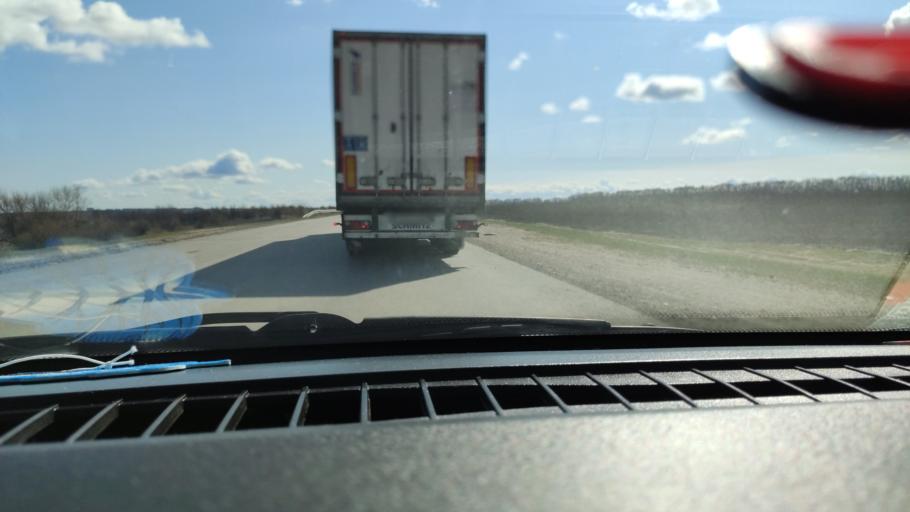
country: RU
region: Samara
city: Varlamovo
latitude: 53.1200
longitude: 48.3297
